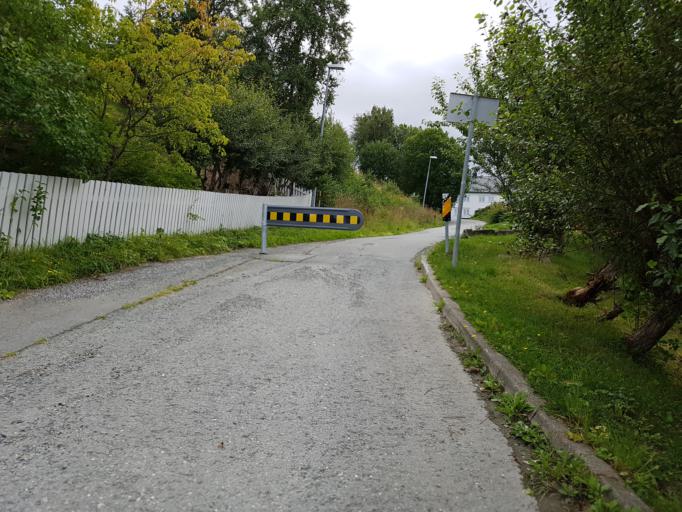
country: NO
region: Sor-Trondelag
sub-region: Trondheim
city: Trondheim
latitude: 63.3971
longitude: 10.4138
